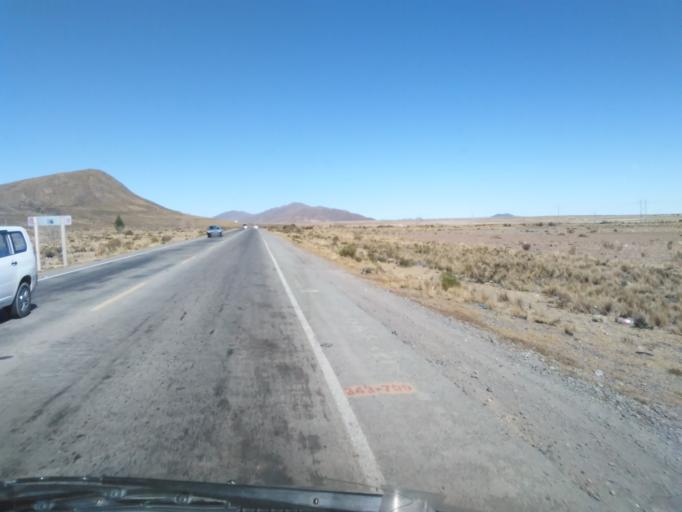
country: BO
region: Oruro
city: Machacamarca
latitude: -18.1057
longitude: -67.0066
